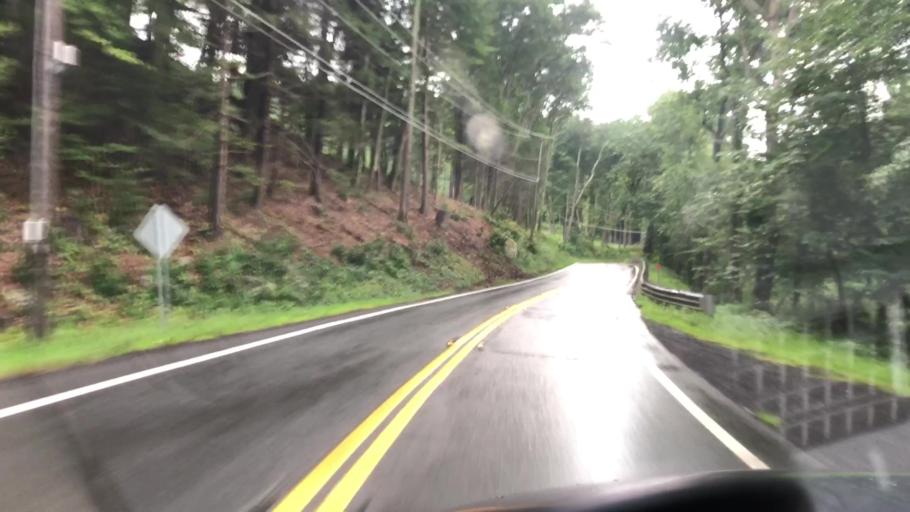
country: US
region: Massachusetts
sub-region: Hampshire County
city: Westhampton
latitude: 42.2605
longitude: -72.8637
